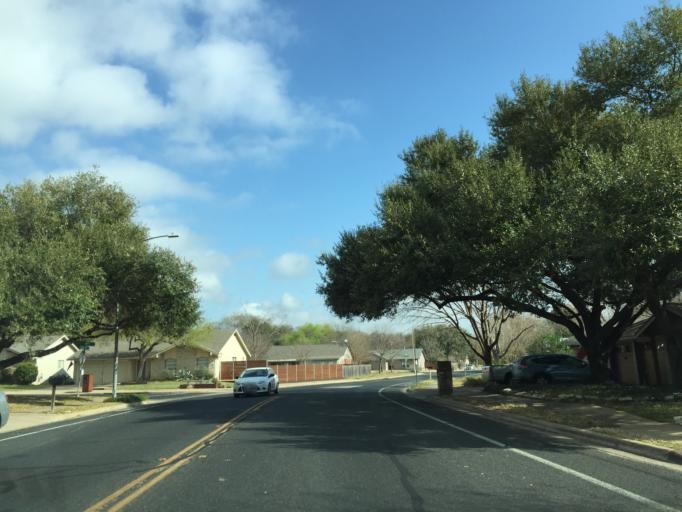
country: US
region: Texas
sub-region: Williamson County
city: Jollyville
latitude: 30.4095
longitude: -97.7370
